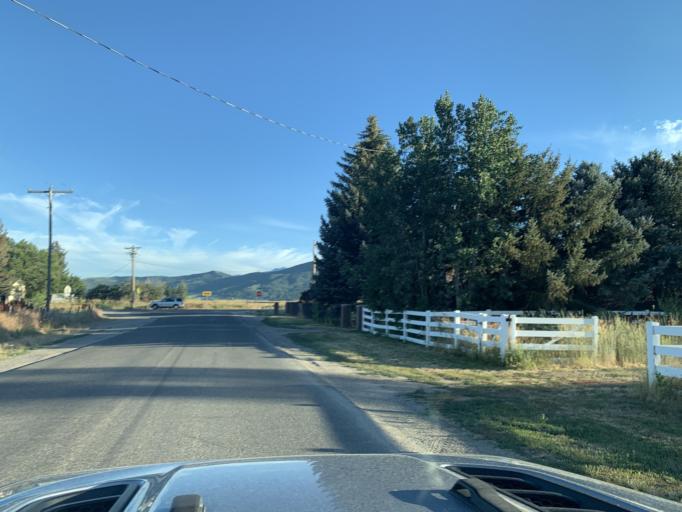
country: US
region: Utah
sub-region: Weber County
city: Wolf Creek
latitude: 41.2941
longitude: -111.8105
